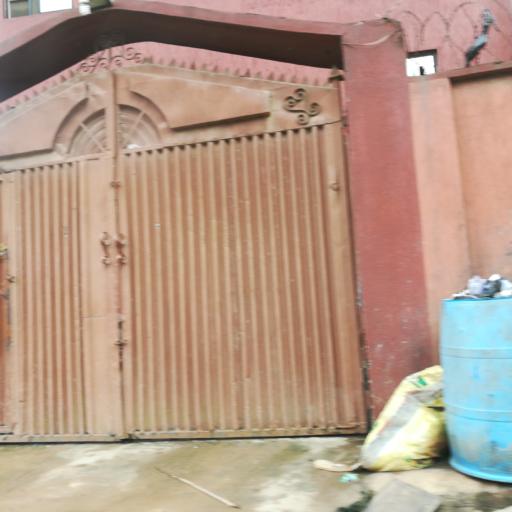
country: NG
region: Lagos
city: Agege
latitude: 6.6070
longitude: 3.3052
